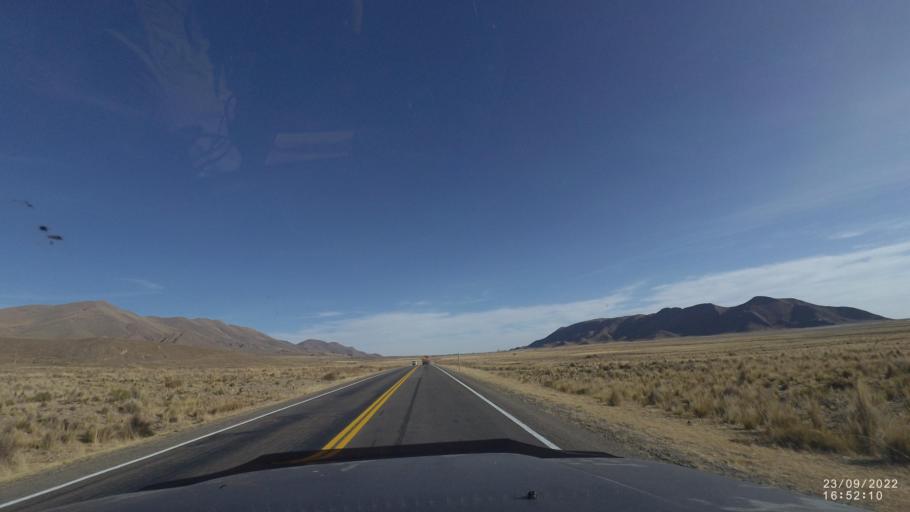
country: BO
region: Oruro
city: Poopo
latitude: -18.4271
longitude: -66.9740
